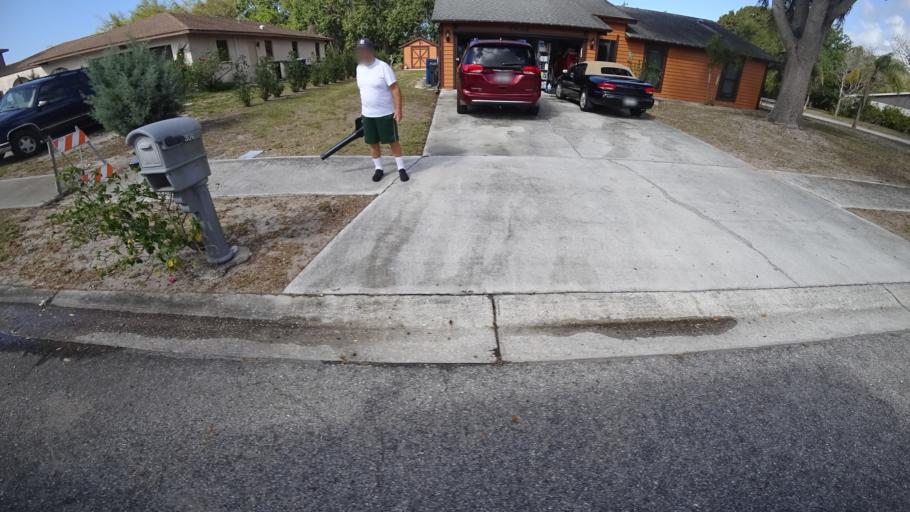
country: US
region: Florida
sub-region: Manatee County
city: Whitfield
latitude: 27.4114
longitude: -82.5631
